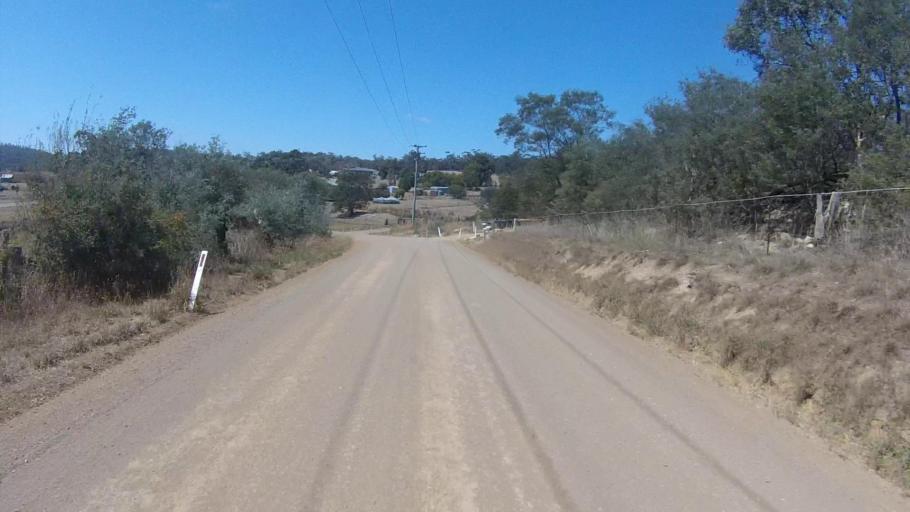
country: AU
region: Tasmania
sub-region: Sorell
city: Sorell
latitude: -42.8255
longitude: 147.6420
